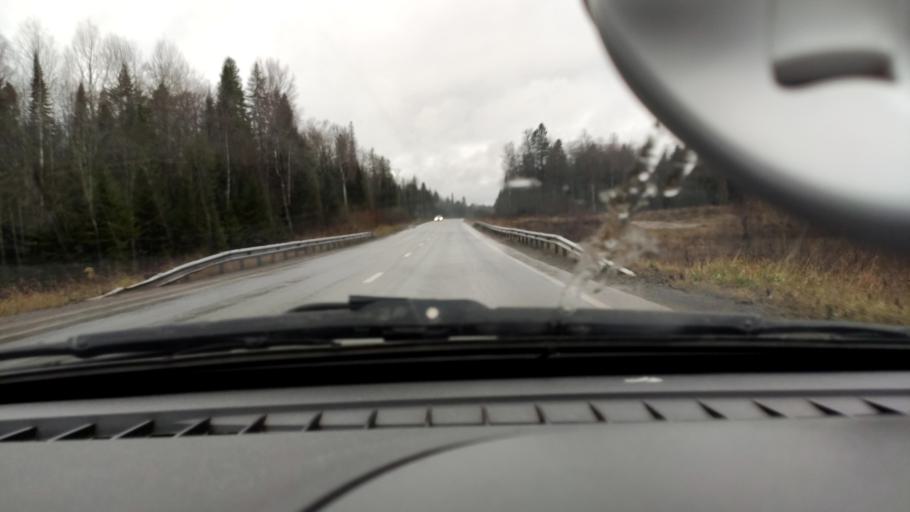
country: RU
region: Perm
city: Novyye Lyady
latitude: 58.0285
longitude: 56.4996
